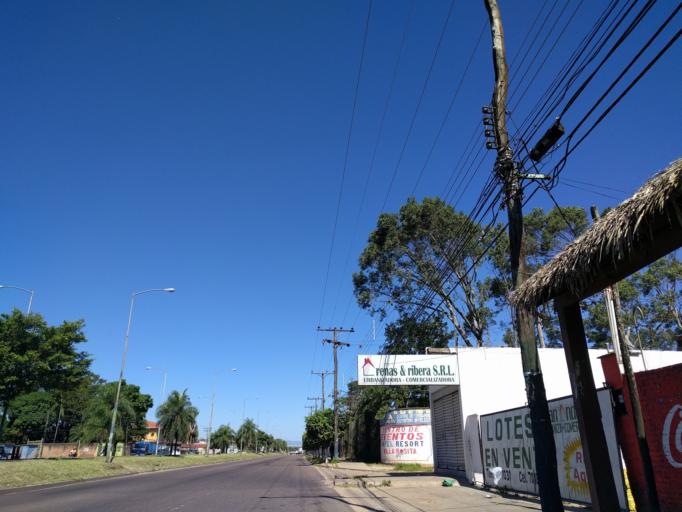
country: BO
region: Santa Cruz
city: Santa Cruz de la Sierra
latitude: -17.8236
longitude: -63.2217
